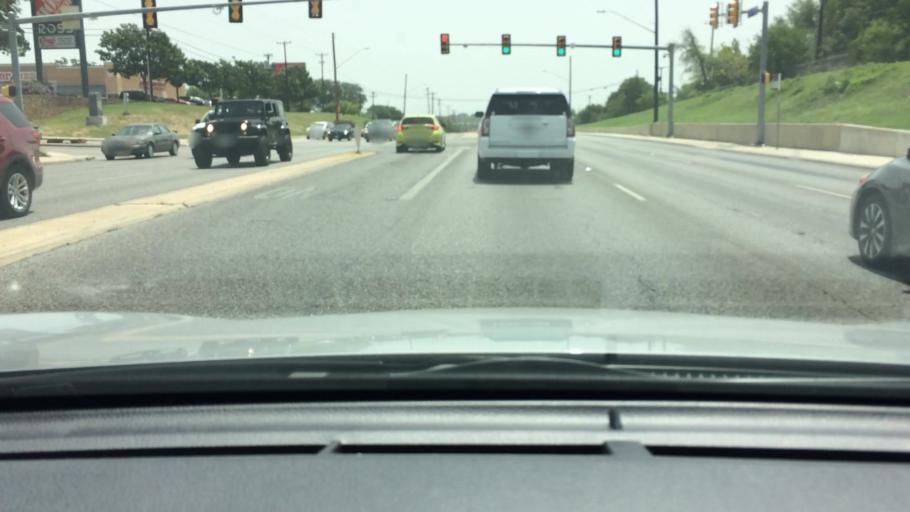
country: US
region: Texas
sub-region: Bexar County
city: San Antonio
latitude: 29.3517
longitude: -98.4409
